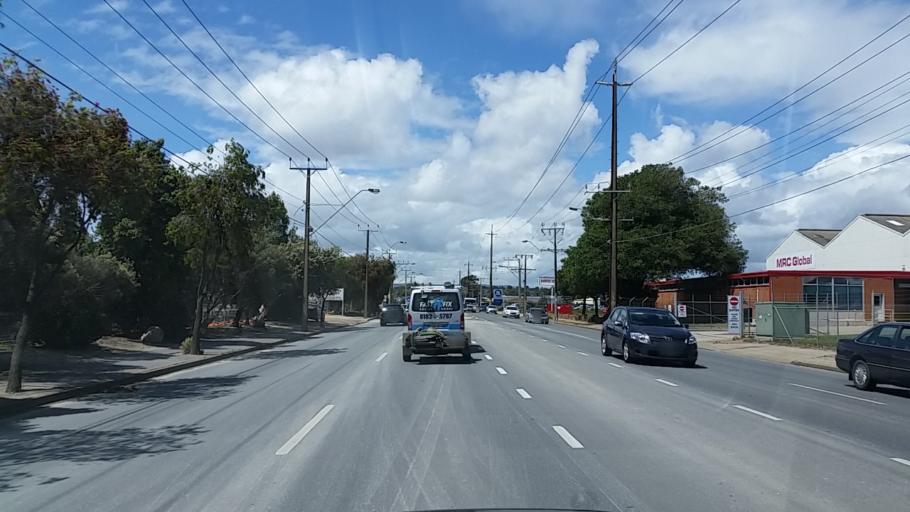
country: AU
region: South Australia
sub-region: Port Adelaide Enfield
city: Blair Athol
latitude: -34.8487
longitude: 138.5873
